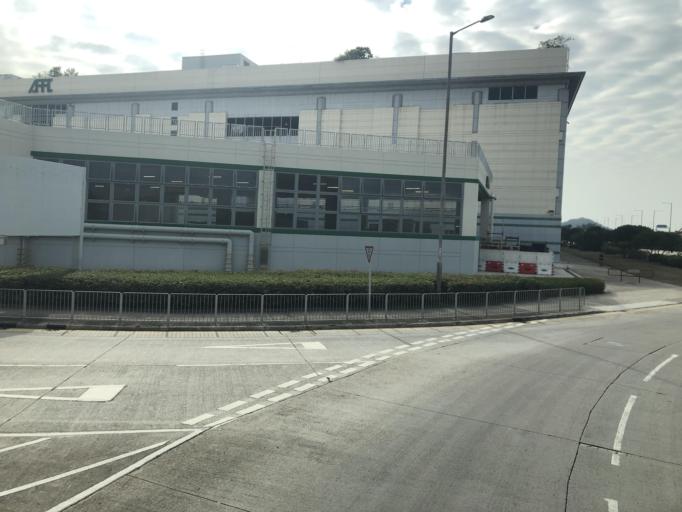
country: HK
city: Tai O
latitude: 22.2958
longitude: 113.9272
